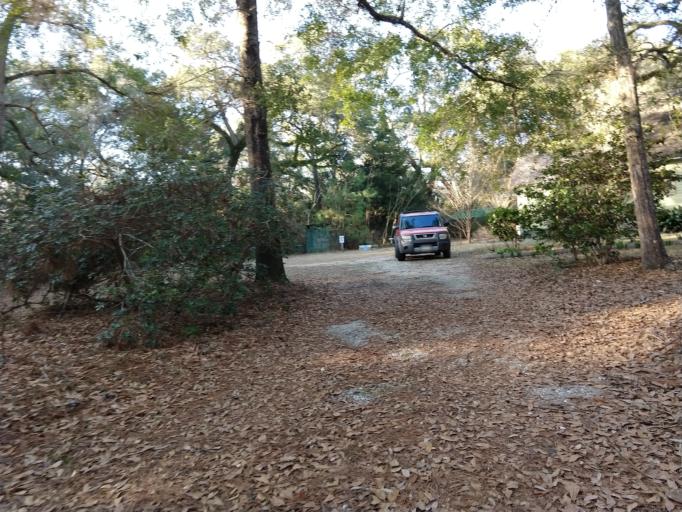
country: US
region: Mississippi
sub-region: Jackson County
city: Ocean Springs
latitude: 30.4166
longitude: -88.7964
